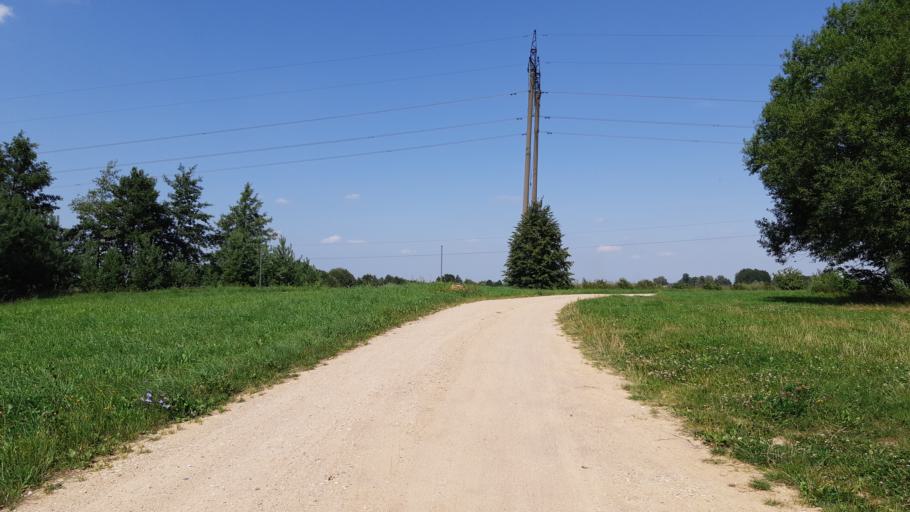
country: LT
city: Virbalis
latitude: 54.6183
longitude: 22.8035
